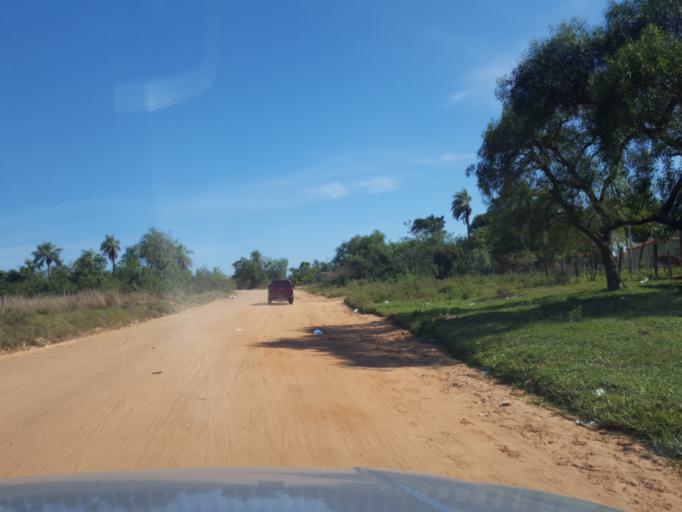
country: PY
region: Cordillera
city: Tobati
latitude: -25.2543
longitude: -57.1026
